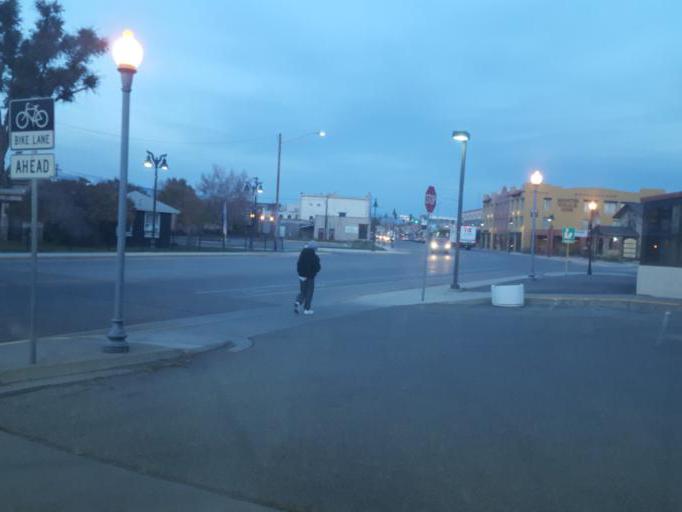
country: US
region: Colorado
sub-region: Rio Grande County
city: Monte Vista
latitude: 37.5804
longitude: -106.1446
